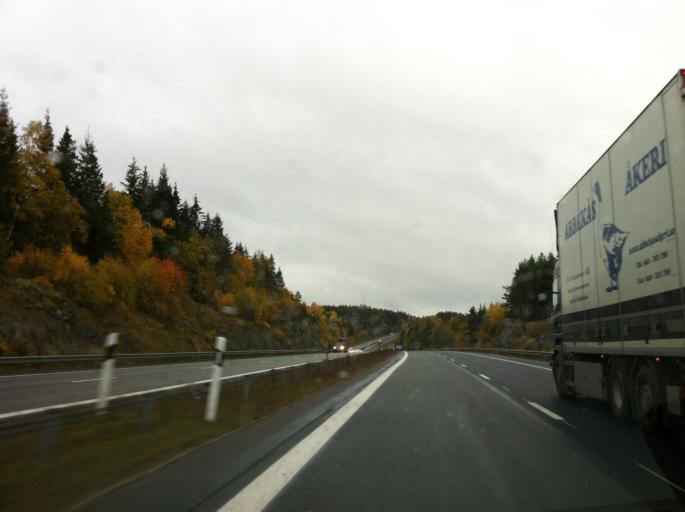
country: SE
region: Joenkoeping
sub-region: Jonkopings Kommun
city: Kaxholmen
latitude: 57.9521
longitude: 14.3468
